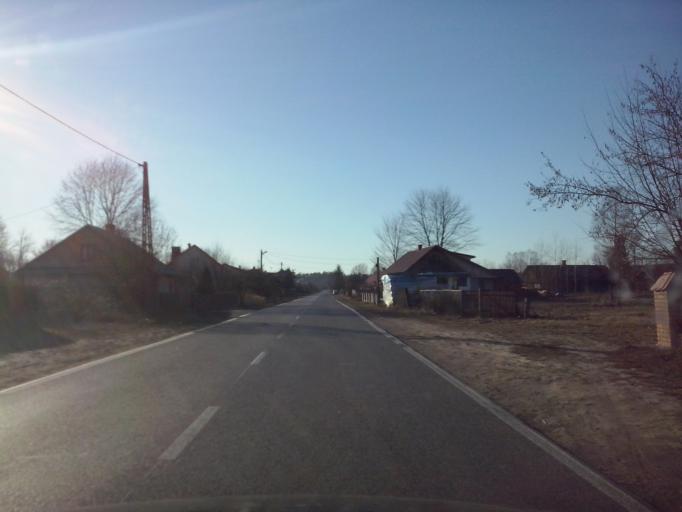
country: PL
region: Subcarpathian Voivodeship
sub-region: Powiat nizanski
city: Harasiuki
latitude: 50.5185
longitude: 22.4789
